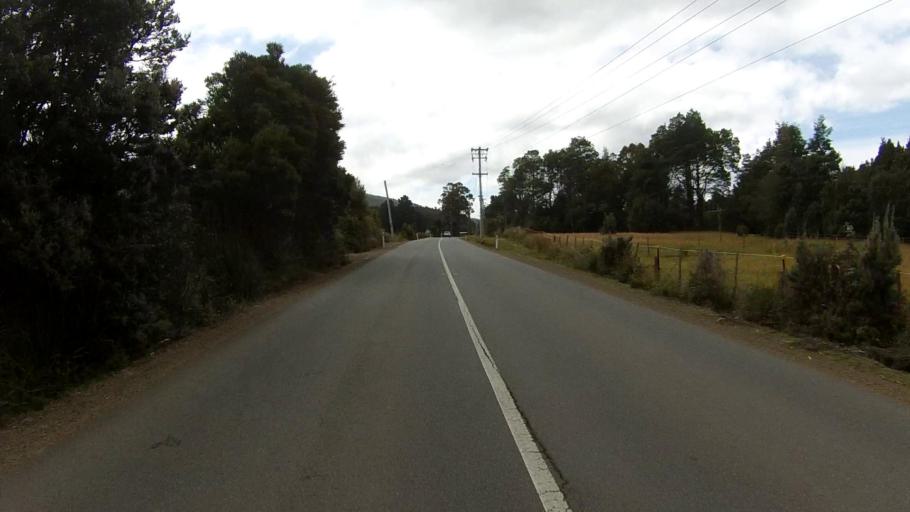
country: AU
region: Tasmania
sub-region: Kingborough
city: Kettering
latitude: -43.1203
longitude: 147.1852
